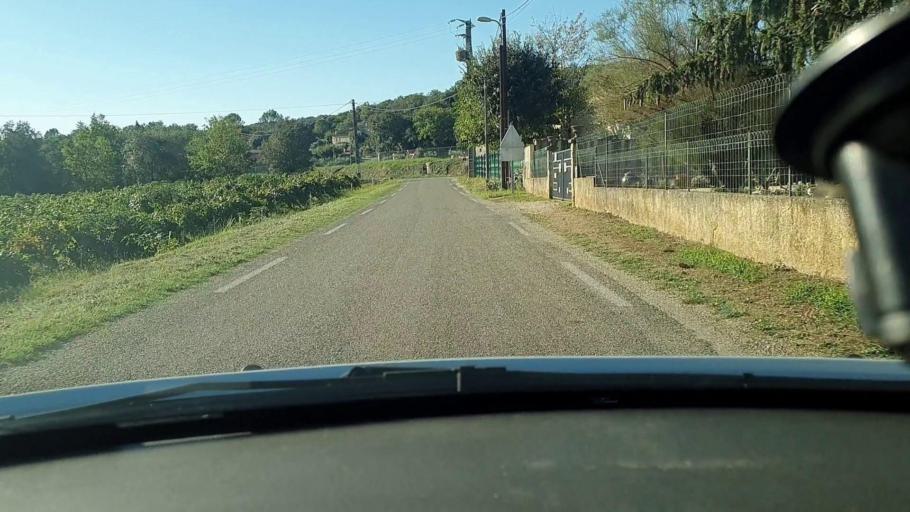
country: FR
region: Languedoc-Roussillon
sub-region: Departement du Gard
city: Goudargues
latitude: 44.2337
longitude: 4.4424
